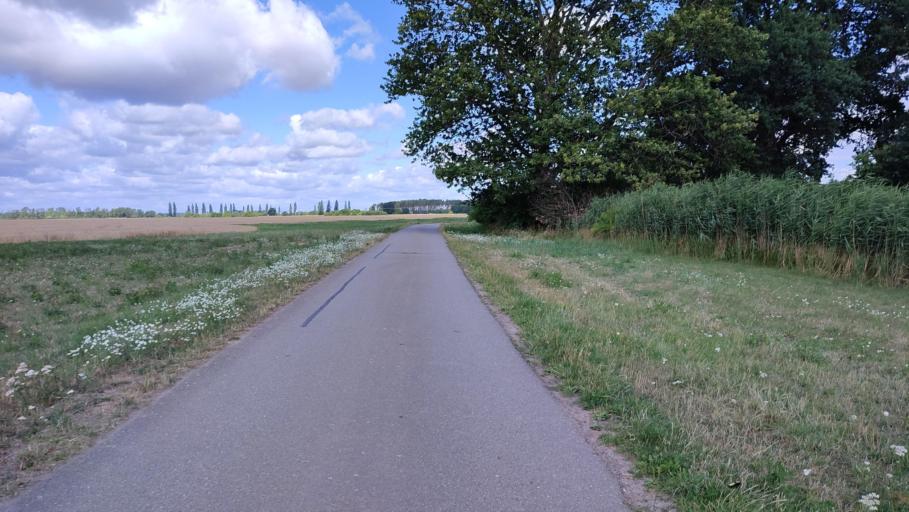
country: DE
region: Lower Saxony
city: Neu Darchau
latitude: 53.2261
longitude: 10.9817
